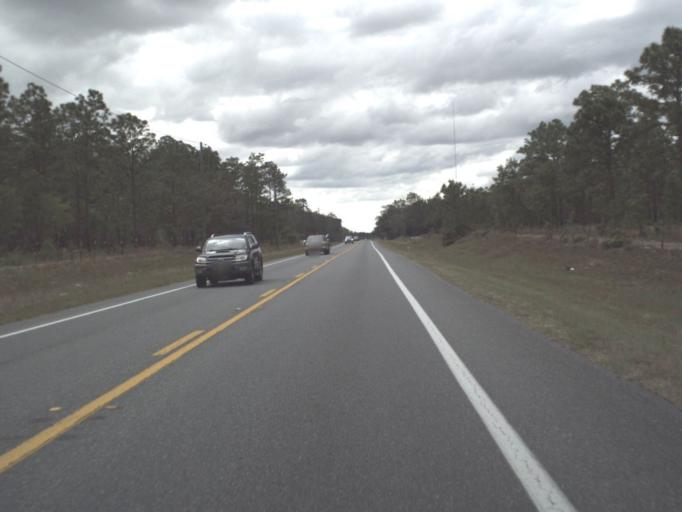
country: US
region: Florida
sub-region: Marion County
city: Ocala
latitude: 29.2471
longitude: -82.0603
